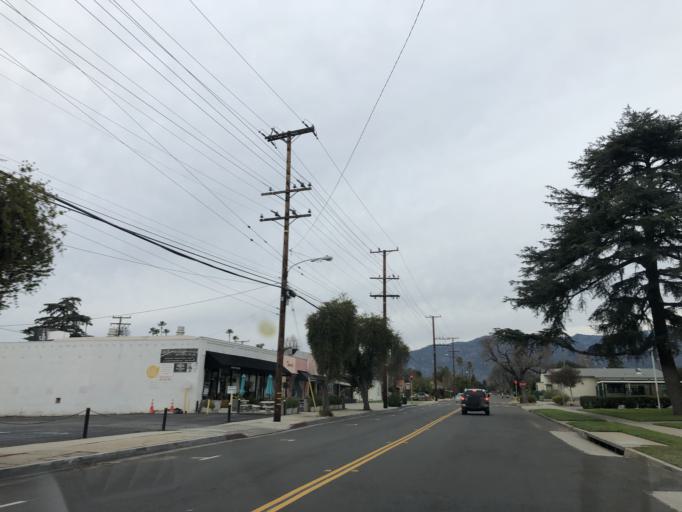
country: US
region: California
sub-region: Los Angeles County
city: San Gabriel
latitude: 34.1064
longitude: -118.1041
